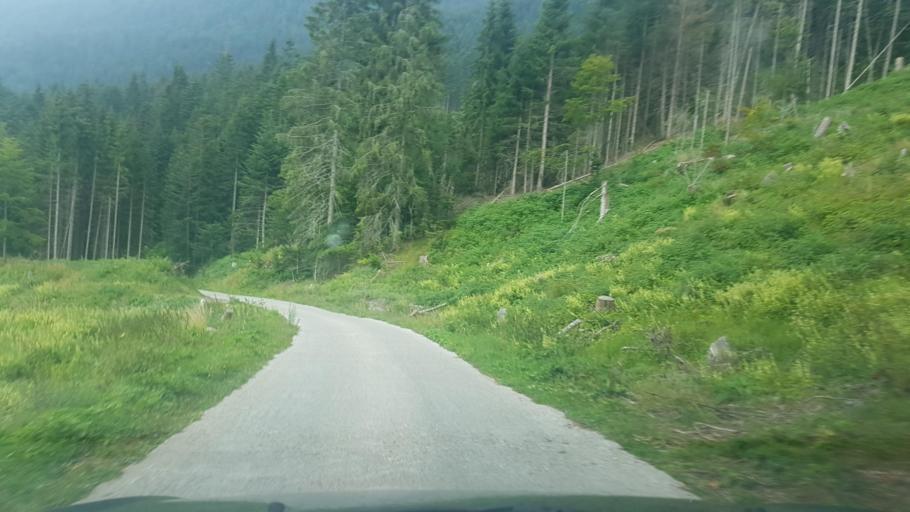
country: IT
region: Friuli Venezia Giulia
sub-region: Provincia di Udine
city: Rigolato
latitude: 46.5516
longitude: 12.8218
